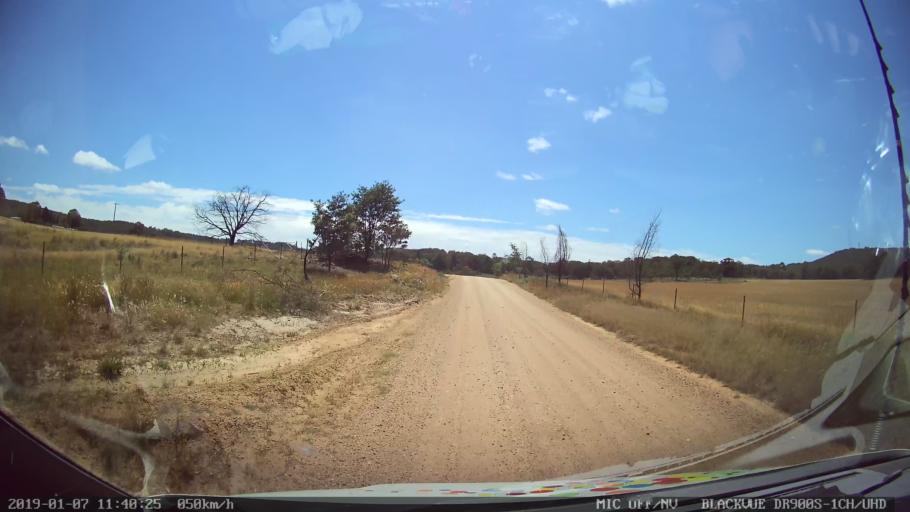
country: AU
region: New South Wales
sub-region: Armidale Dumaresq
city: Armidale
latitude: -30.3639
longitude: 151.5837
